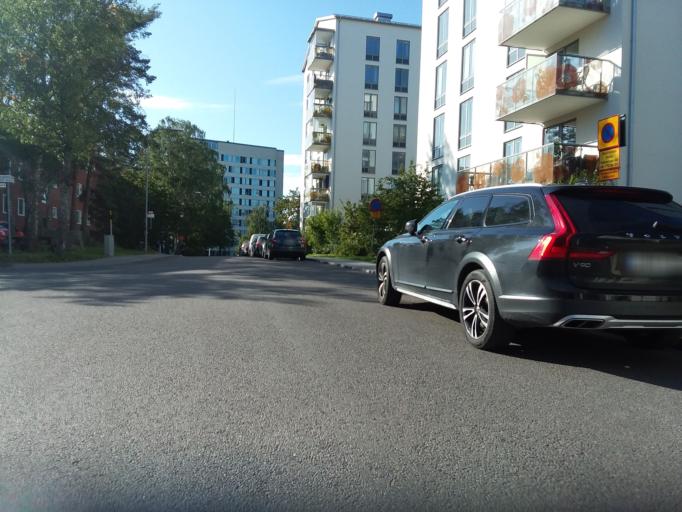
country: SE
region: Stockholm
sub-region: Stockholms Kommun
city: Bromma
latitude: 59.3461
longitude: 17.8784
